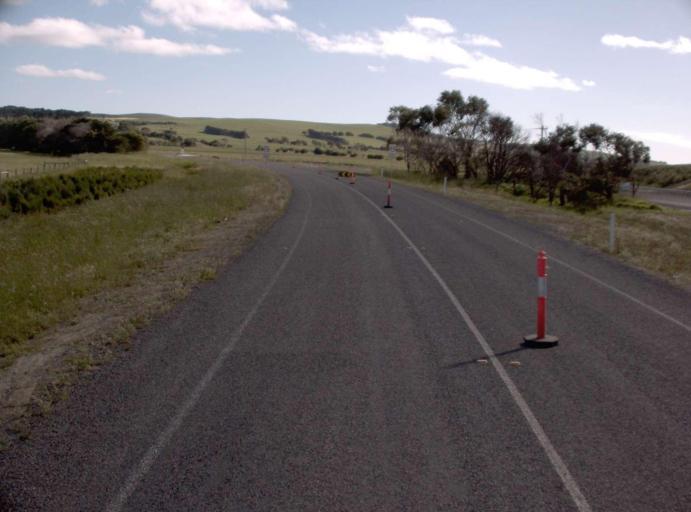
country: AU
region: Victoria
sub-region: Bass Coast
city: North Wonthaggi
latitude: -38.5074
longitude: 145.4518
